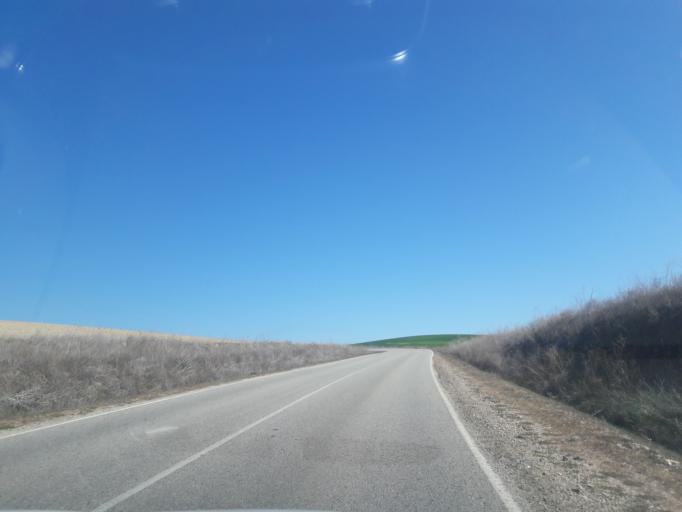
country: ES
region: Castille and Leon
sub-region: Provincia de Salamanca
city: Boveda del Rio Almar
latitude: 40.8630
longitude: -5.1997
